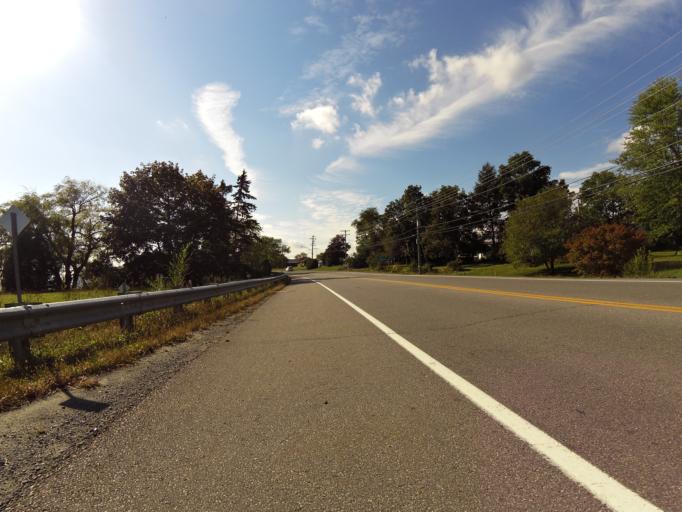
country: CA
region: Ontario
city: Kingston
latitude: 44.2146
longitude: -76.6638
